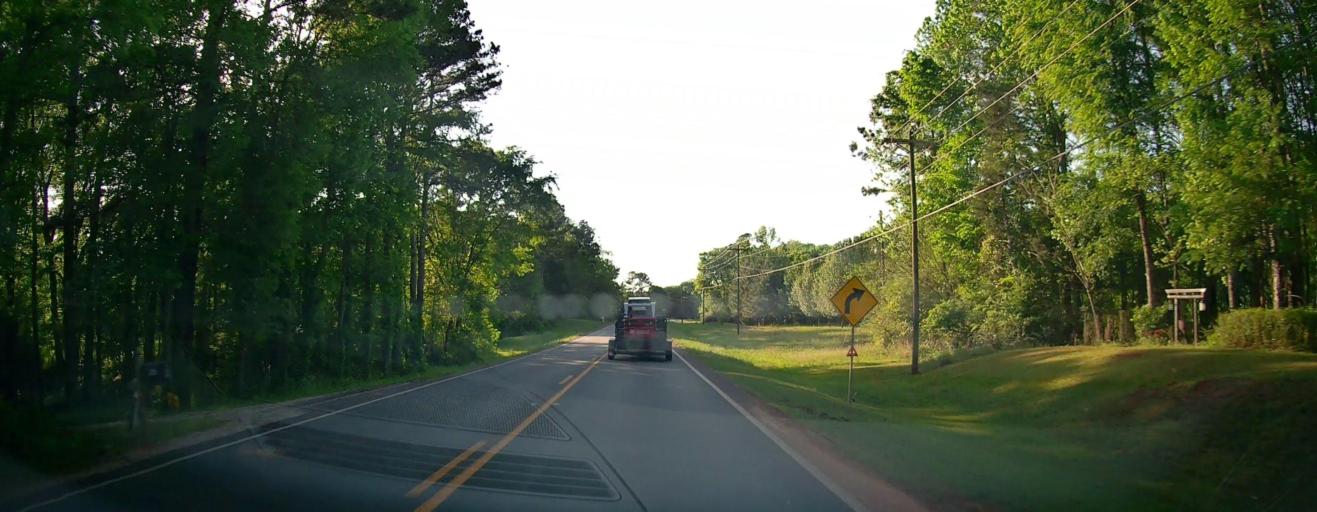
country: US
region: Georgia
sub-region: Putnam County
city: Eatonton
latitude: 33.3107
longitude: -83.4886
